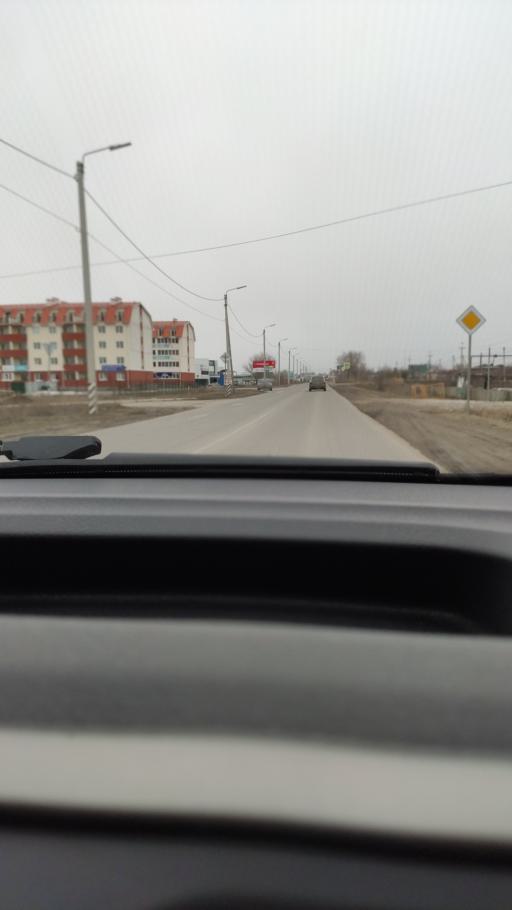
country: RU
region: Samara
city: Podstepki
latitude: 53.5221
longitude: 49.1870
